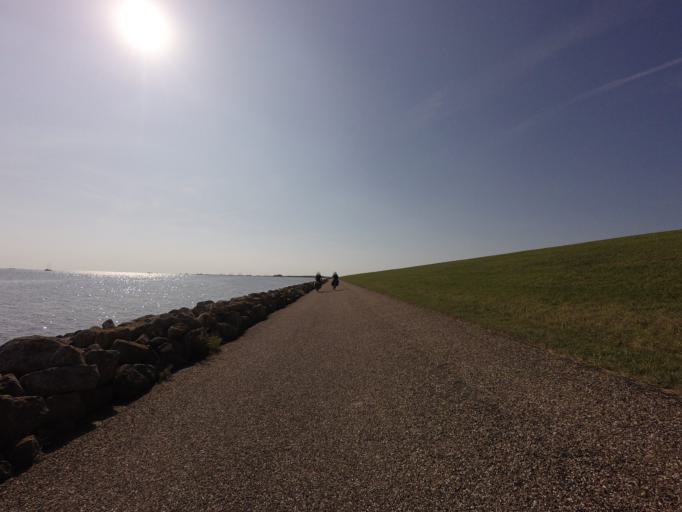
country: NL
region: Friesland
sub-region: Gemeente Schiermonnikoog
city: Schiermonnikoog
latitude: 53.4724
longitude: 6.1829
